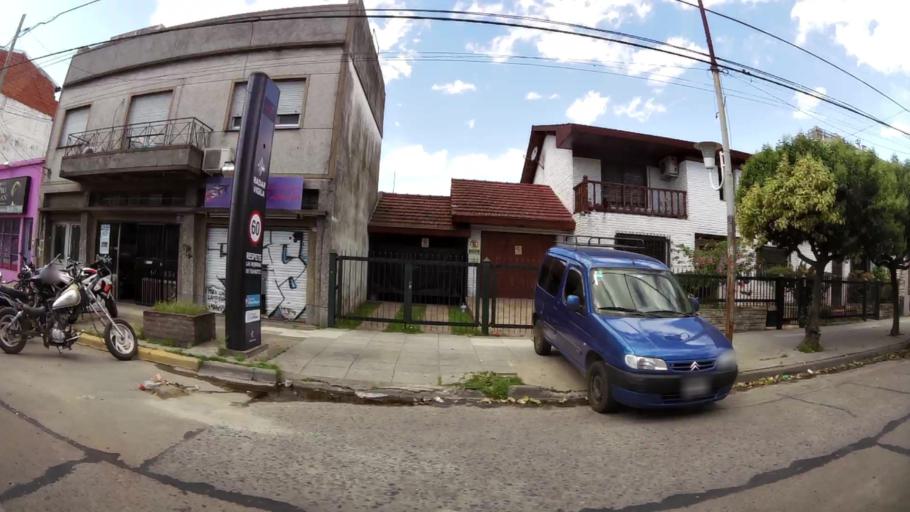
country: AR
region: Buenos Aires
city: San Justo
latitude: -34.6537
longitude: -58.5507
